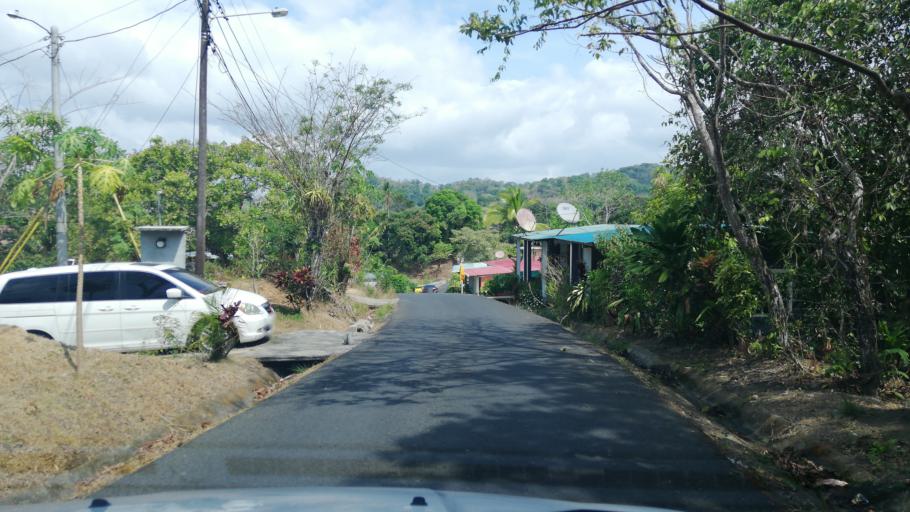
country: PA
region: Panama
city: Alcalde Diaz
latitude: 9.1260
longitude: -79.5647
